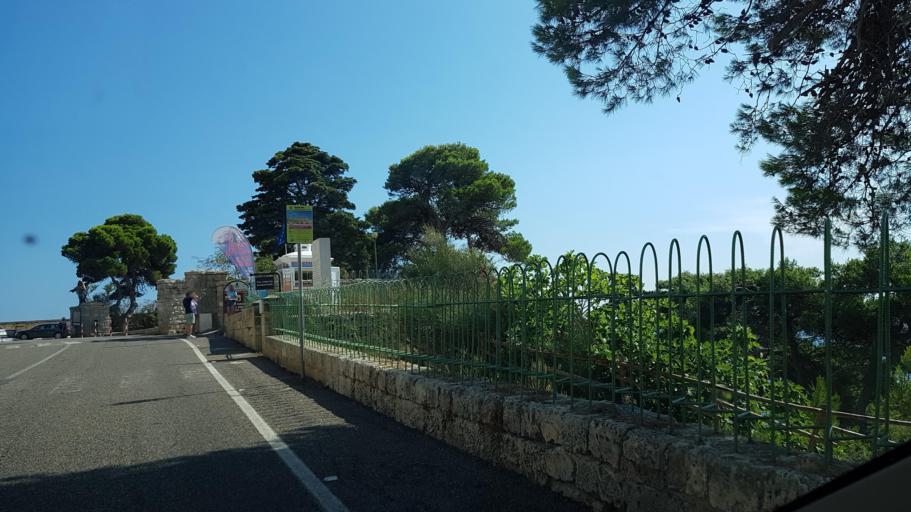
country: IT
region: Apulia
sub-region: Provincia di Lecce
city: Leuca
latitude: 39.7975
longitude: 18.3678
